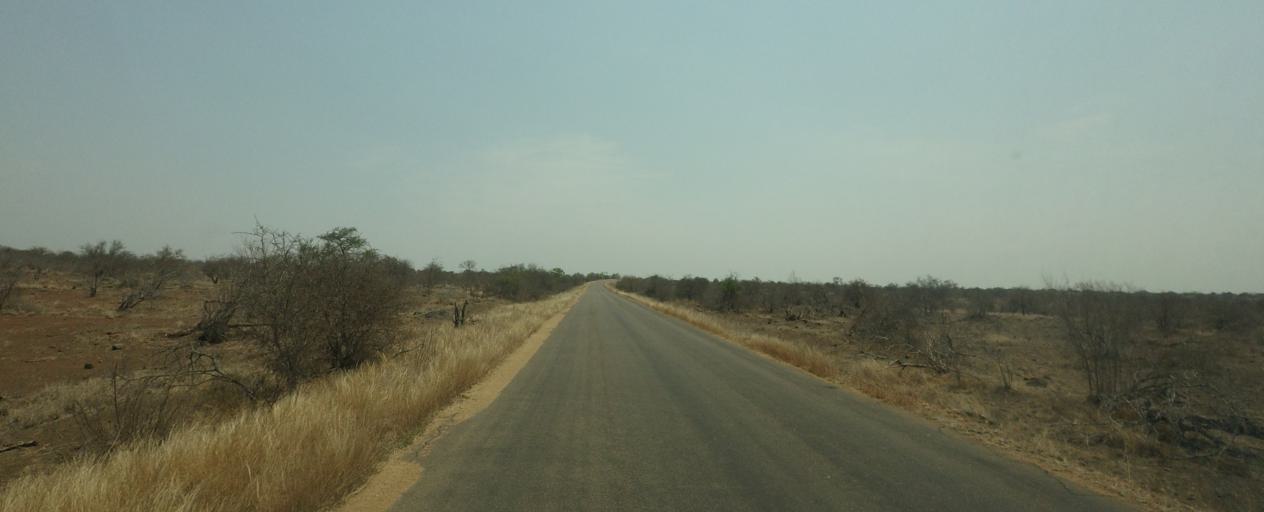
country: ZA
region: Limpopo
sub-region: Mopani District Municipality
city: Phalaborwa
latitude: -24.1187
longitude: 31.6964
